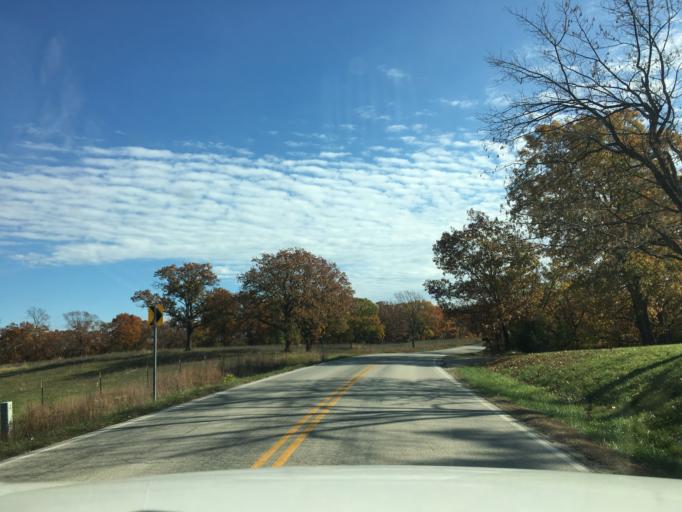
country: US
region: Missouri
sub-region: Maries County
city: Belle
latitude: 38.3088
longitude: -91.7369
